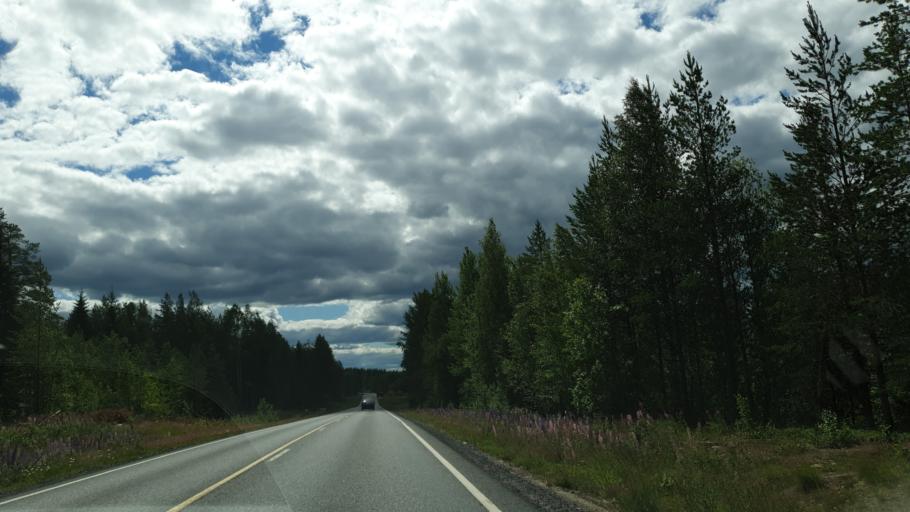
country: FI
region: Kainuu
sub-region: Kehys-Kainuu
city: Kuhmo
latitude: 64.0846
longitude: 29.4839
